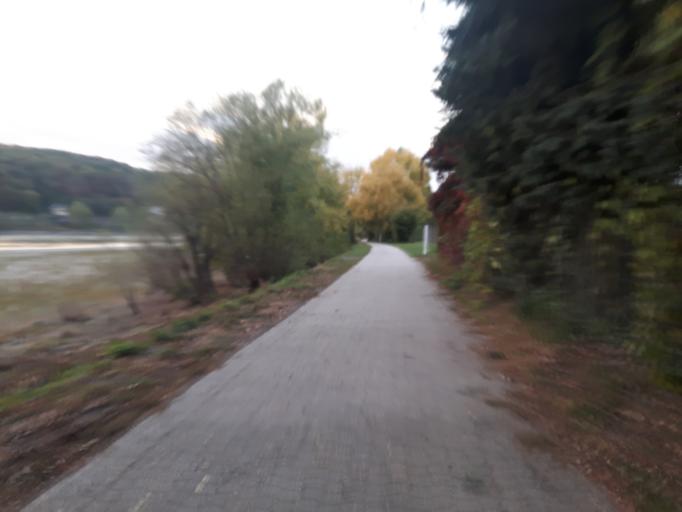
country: DE
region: Rheinland-Pfalz
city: Remagen
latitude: 50.5848
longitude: 7.2262
